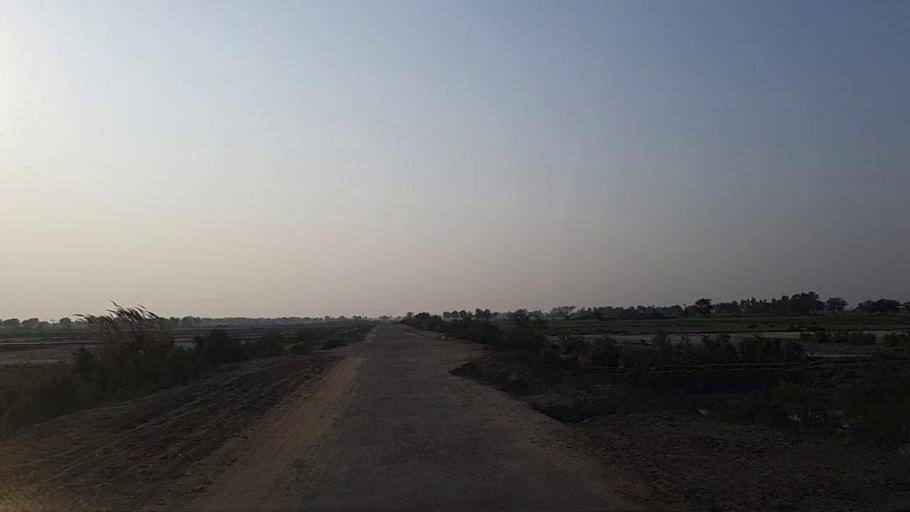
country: PK
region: Sindh
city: Daur
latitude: 26.4069
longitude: 68.3924
